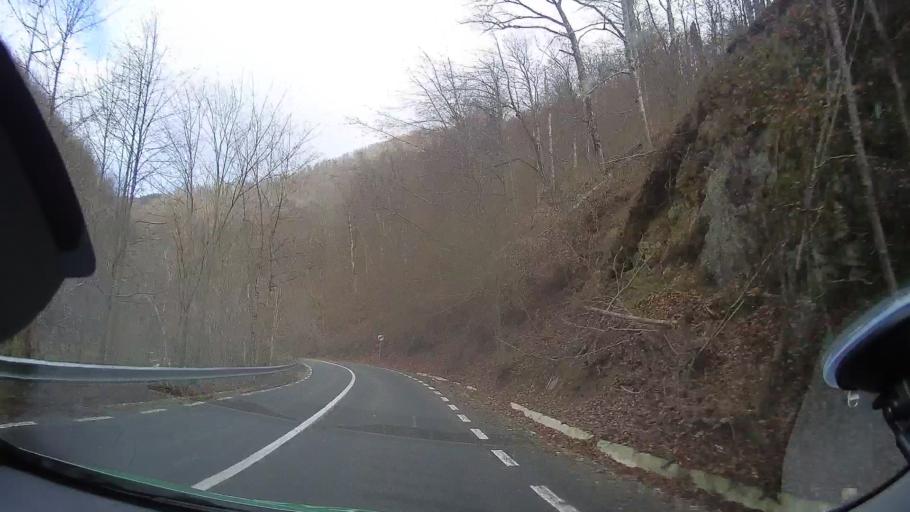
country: RO
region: Cluj
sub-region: Comuna Valea Ierii
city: Valea Ierii
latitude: 46.6335
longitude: 23.3721
